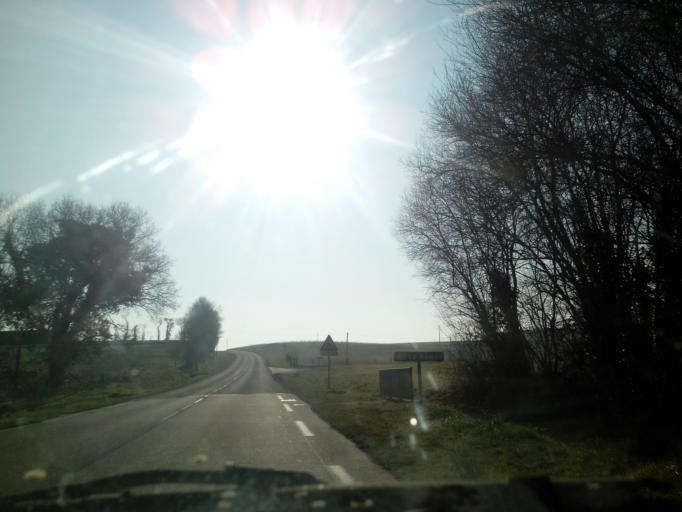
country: FR
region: Brittany
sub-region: Departement des Cotes-d'Armor
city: Merdrignac
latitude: 48.1731
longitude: -2.4332
